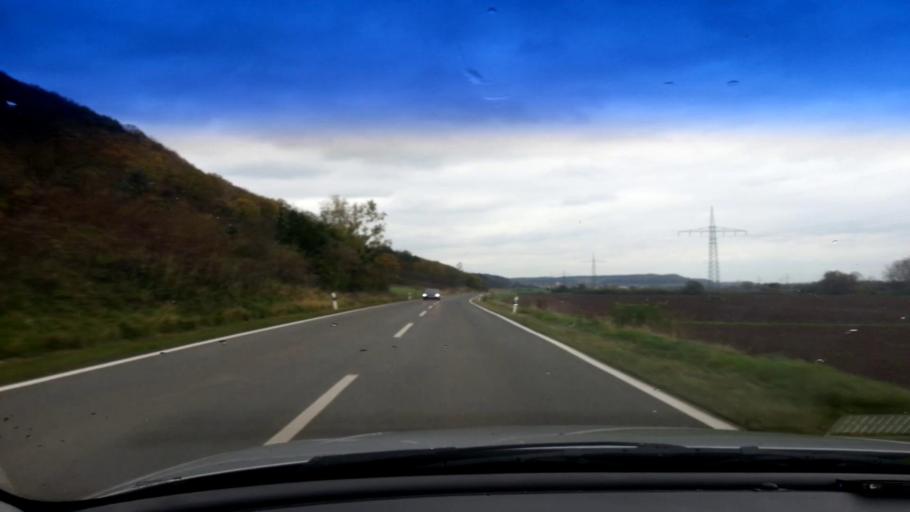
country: DE
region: Bavaria
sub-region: Regierungsbezirk Unterfranken
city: Ebelsbach
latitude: 49.9802
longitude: 10.6872
